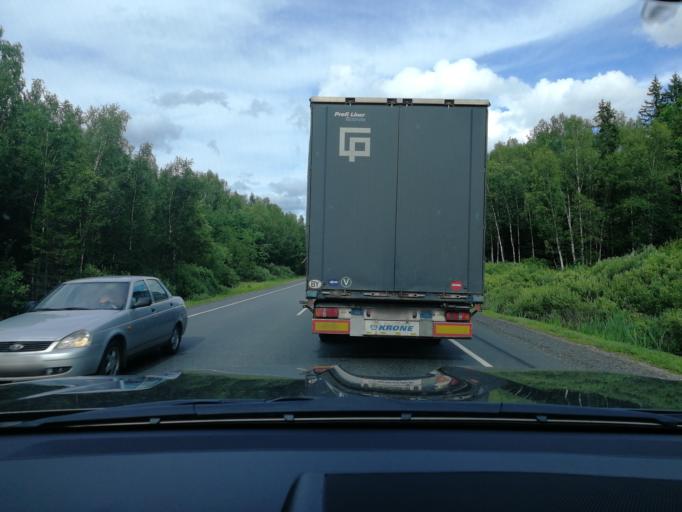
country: RU
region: Moskovskaya
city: Popovo
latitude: 55.0424
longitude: 37.6893
